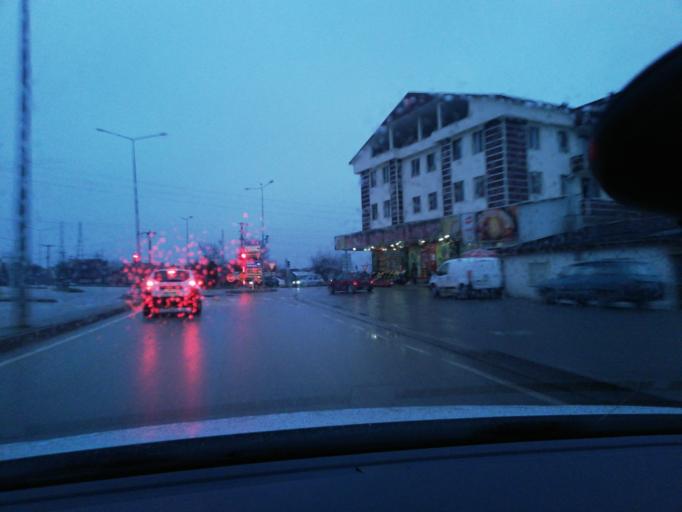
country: TR
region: Bolu
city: Bolu
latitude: 40.7229
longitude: 31.6120
